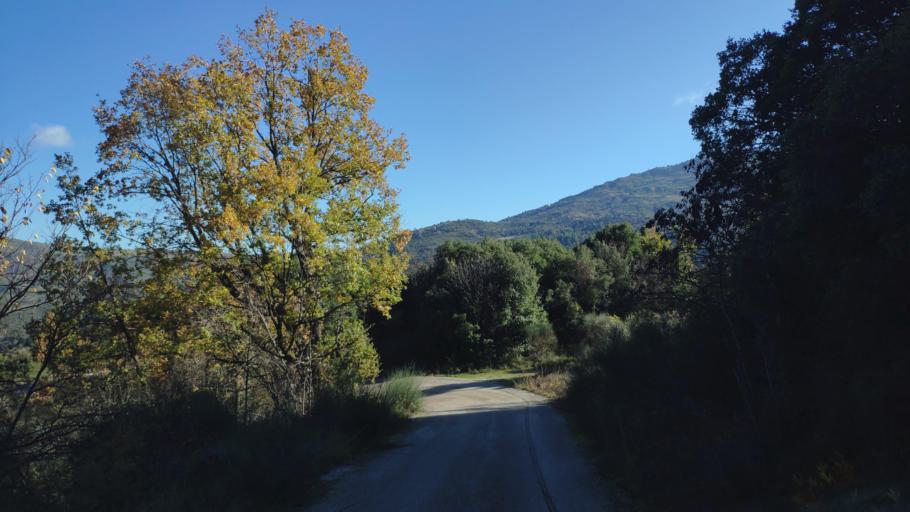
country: GR
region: West Greece
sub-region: Nomos Achaias
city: Aiyira
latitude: 38.0521
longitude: 22.4496
